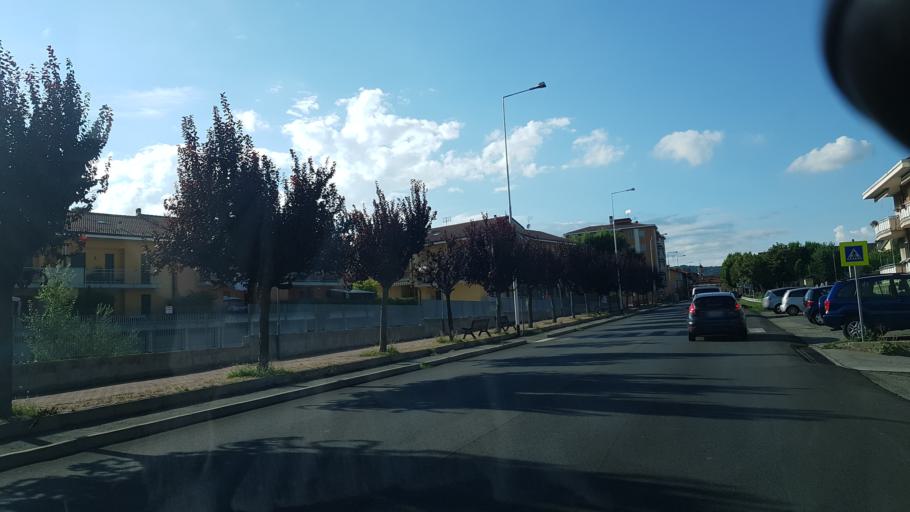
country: IT
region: Piedmont
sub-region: Provincia di Cuneo
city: Costiglione Saluzzo
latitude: 44.5593
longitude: 7.4883
